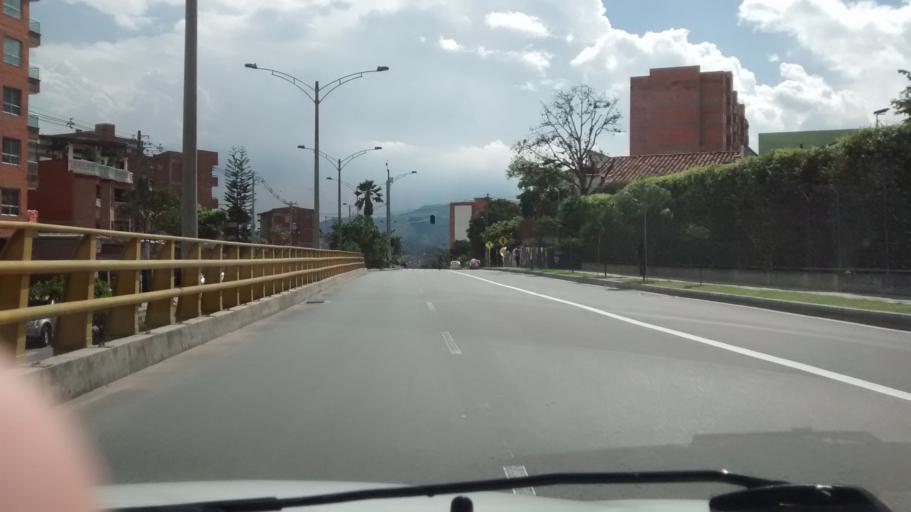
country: CO
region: Antioquia
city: Medellin
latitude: 6.2810
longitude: -75.5869
